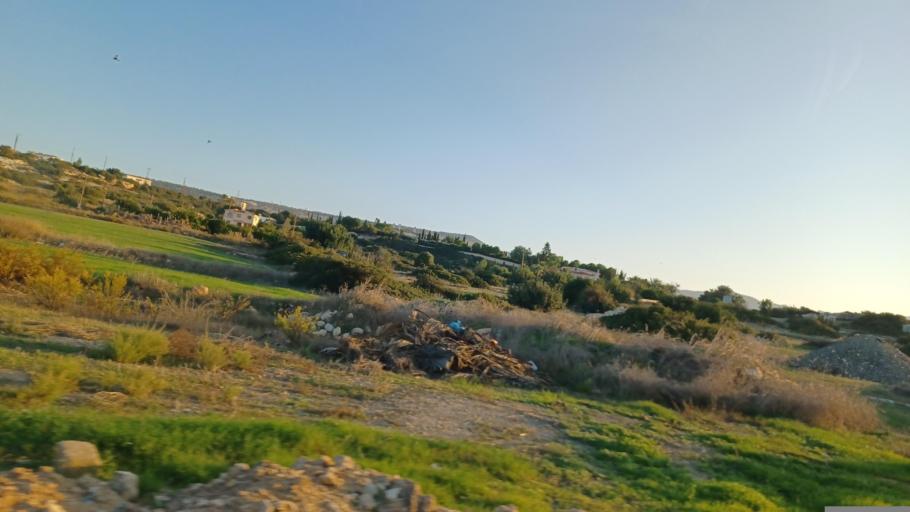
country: CY
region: Pafos
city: Pegeia
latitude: 34.8687
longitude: 32.3529
